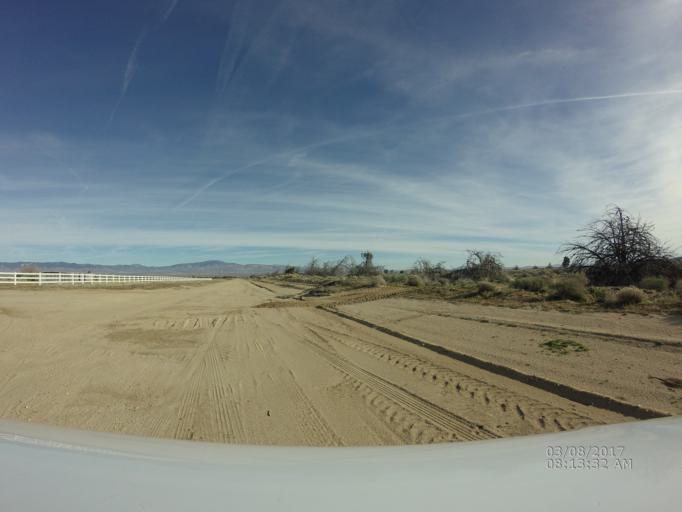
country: US
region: California
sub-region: Los Angeles County
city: Green Valley
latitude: 34.7567
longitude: -118.4488
